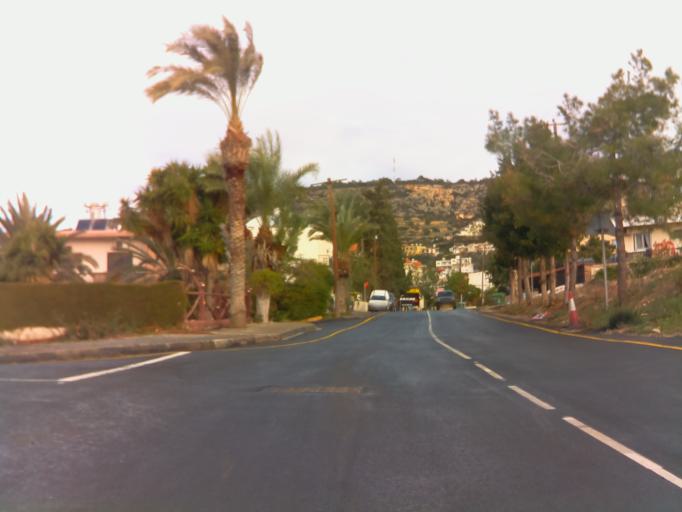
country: CY
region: Pafos
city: Pegeia
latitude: 34.8775
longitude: 32.3801
